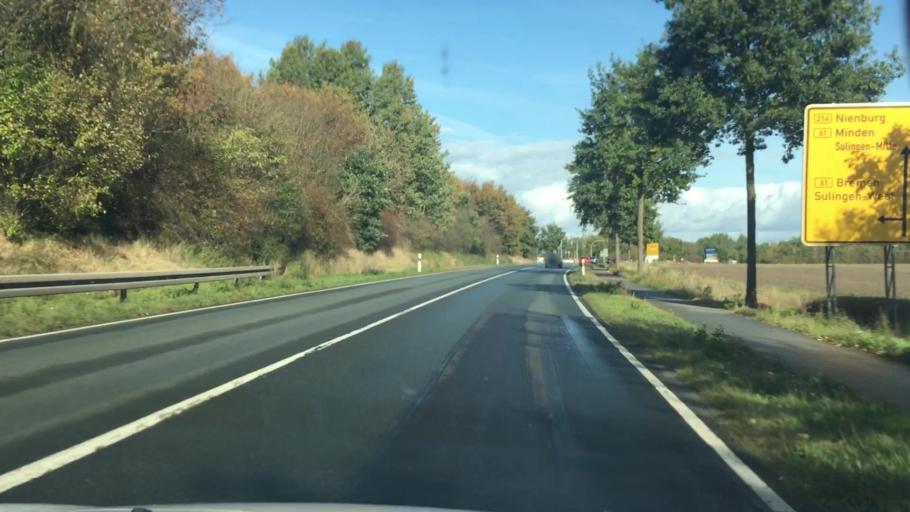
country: DE
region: Lower Saxony
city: Sulingen
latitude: 52.6688
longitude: 8.7805
